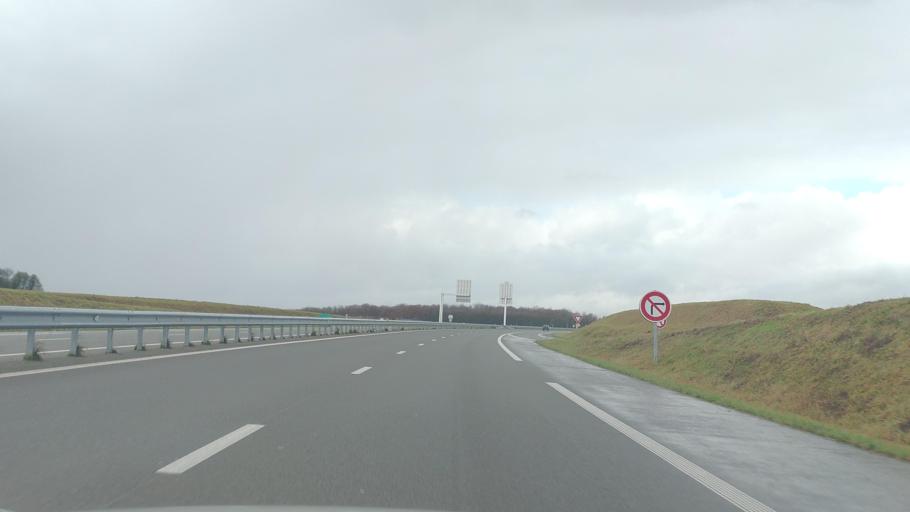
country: FR
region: Picardie
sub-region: Departement de l'Oise
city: Troissereux
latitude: 49.4688
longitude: 2.0755
